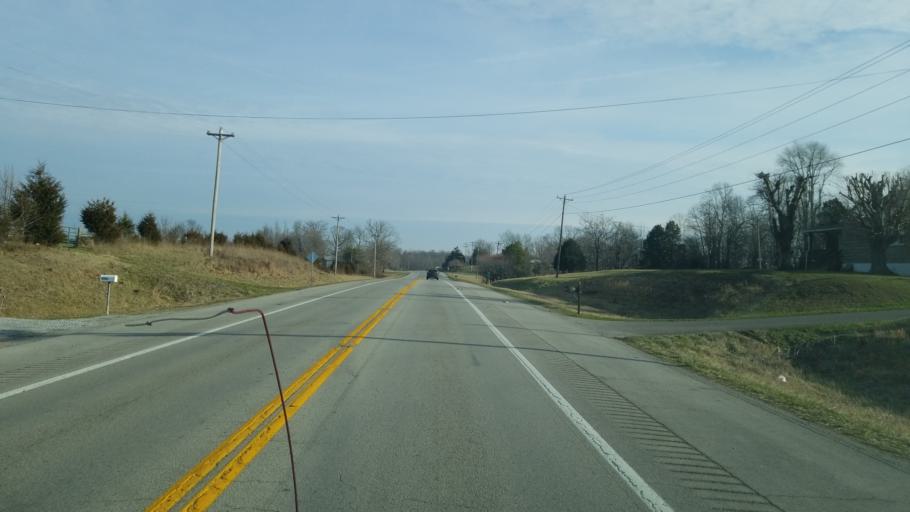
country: US
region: Kentucky
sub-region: Russell County
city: Russell Springs
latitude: 37.1067
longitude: -85.0559
